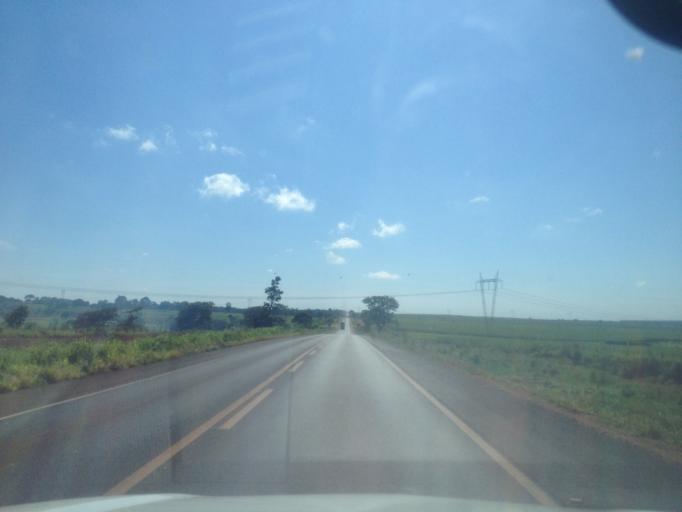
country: BR
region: Minas Gerais
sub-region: Santa Vitoria
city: Santa Vitoria
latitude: -19.0471
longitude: -50.4803
